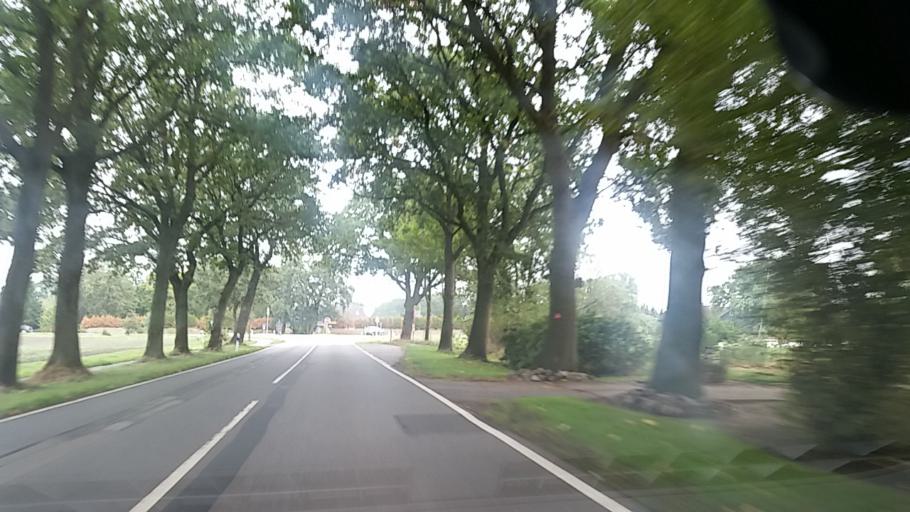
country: DE
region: Schleswig-Holstein
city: Hasenmoor
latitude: 53.8986
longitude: 9.9789
